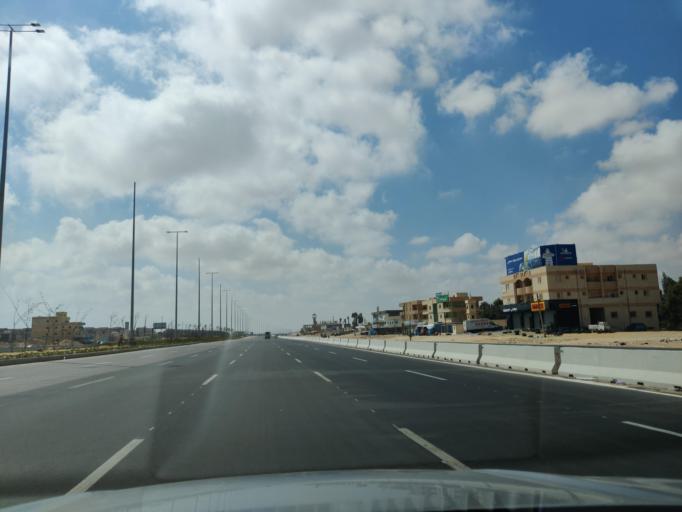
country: EG
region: Muhafazat Matruh
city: Al `Alamayn
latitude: 30.9443
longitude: 28.7788
